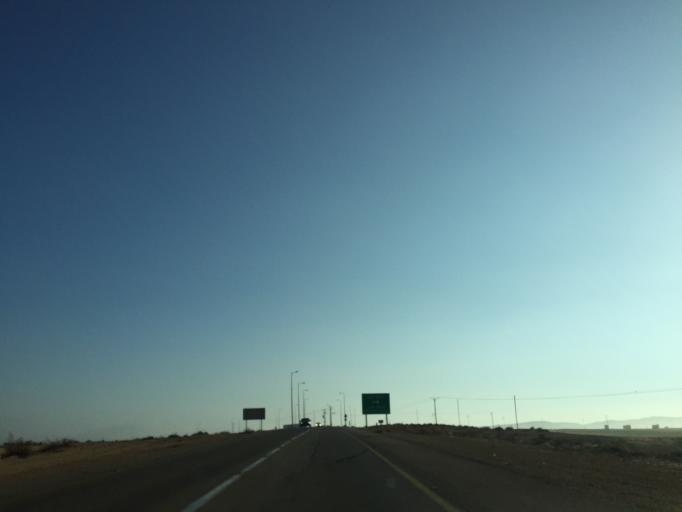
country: IL
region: Southern District
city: Yeroham
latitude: 30.9976
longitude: 34.9379
